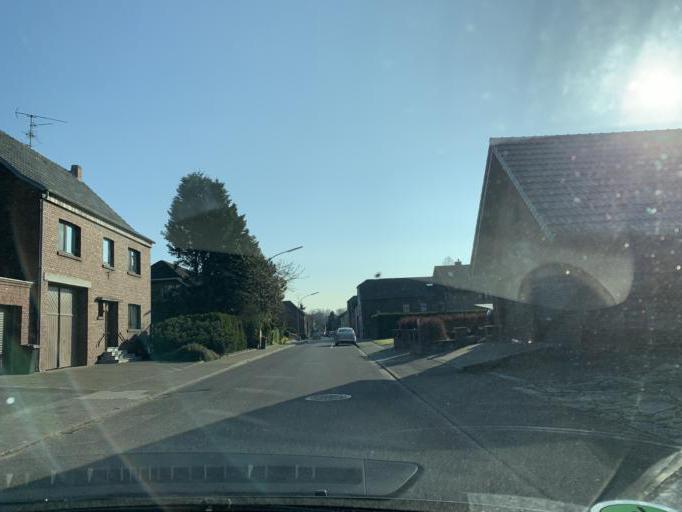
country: DE
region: North Rhine-Westphalia
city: Erkelenz
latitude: 51.0838
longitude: 6.3938
